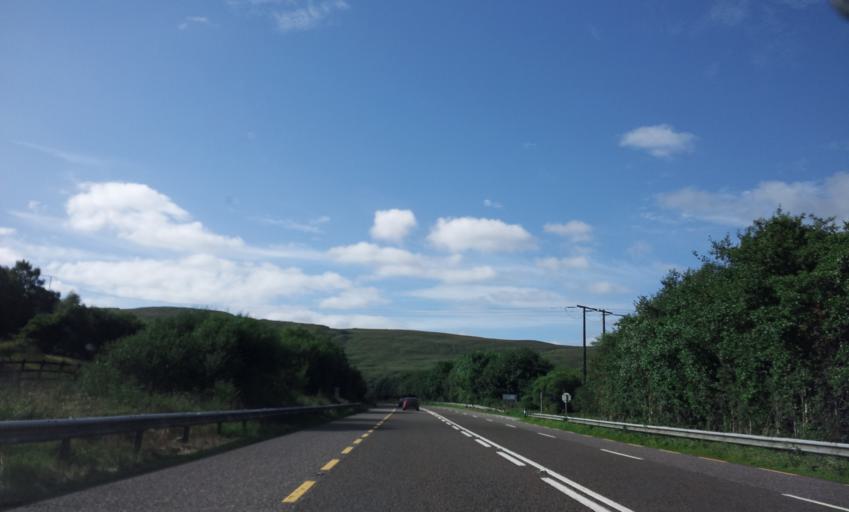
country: IE
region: Munster
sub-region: County Cork
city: Millstreet
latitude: 51.9851
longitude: -9.2825
